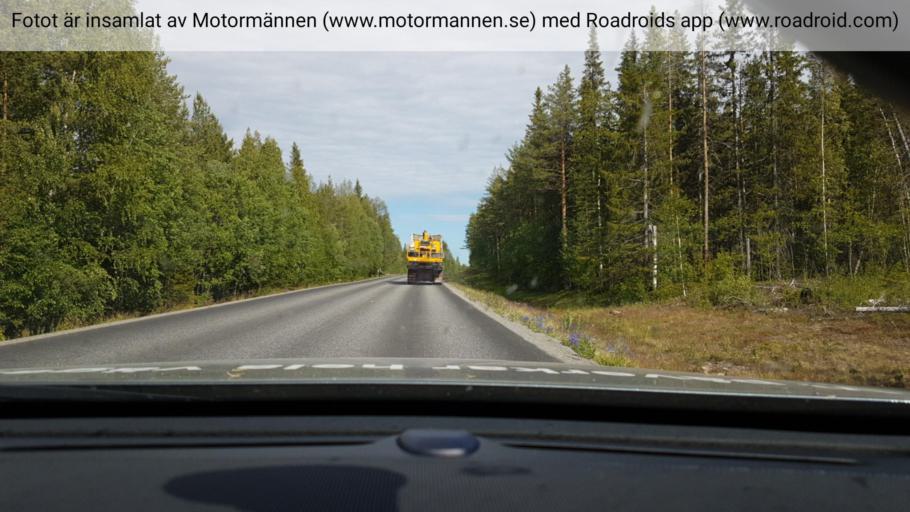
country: SE
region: Vaesterbotten
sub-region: Lycksele Kommun
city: Soderfors
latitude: 64.8306
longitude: 18.0209
